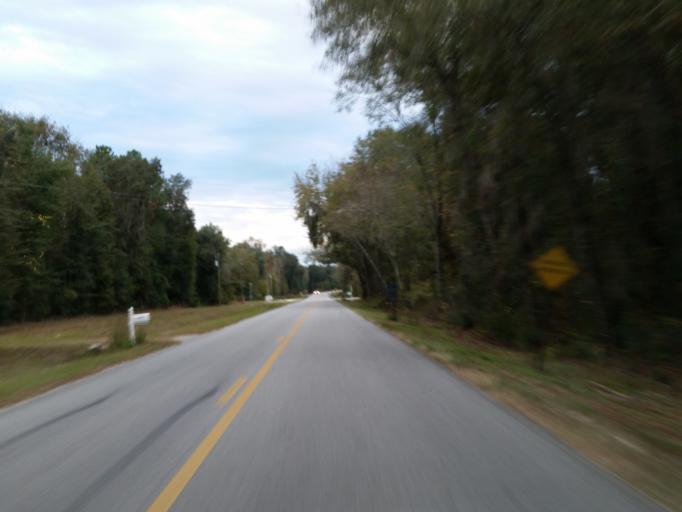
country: US
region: Florida
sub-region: Hamilton County
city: Jasper
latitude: 30.5573
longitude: -83.0993
